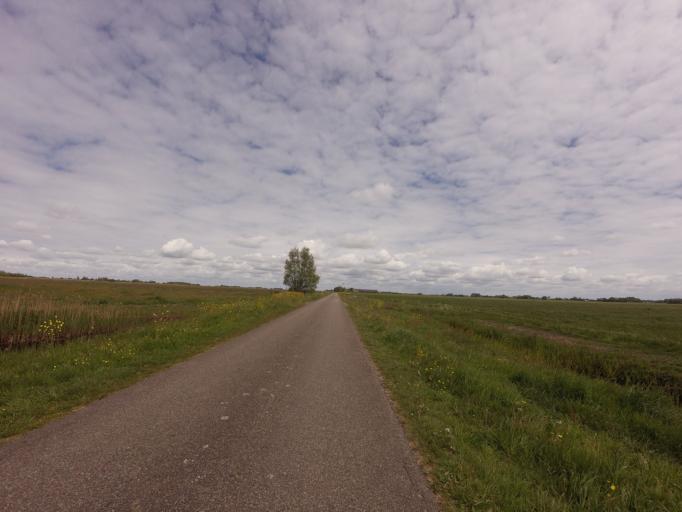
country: NL
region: Friesland
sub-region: Sudwest Fryslan
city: Koudum
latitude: 52.9097
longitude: 5.5033
